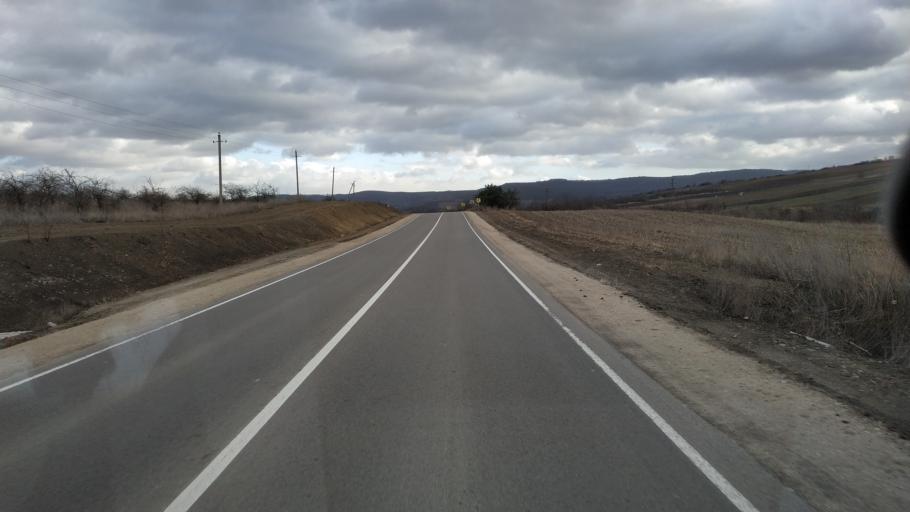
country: MD
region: Calarasi
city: Calarasi
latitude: 47.2683
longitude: 28.2278
